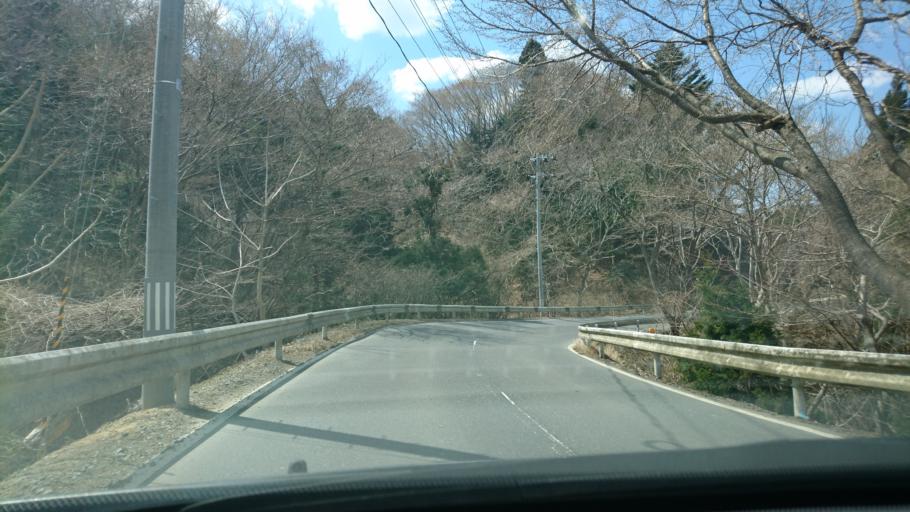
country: JP
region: Miyagi
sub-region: Oshika Gun
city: Onagawa Cho
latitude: 38.4603
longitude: 141.4867
